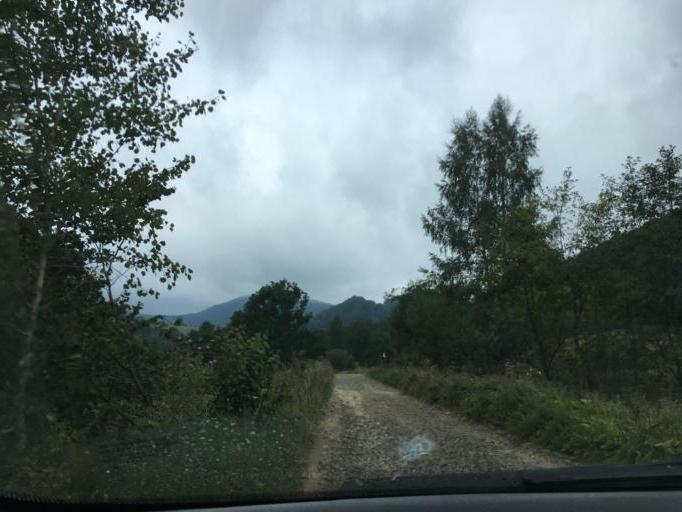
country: PL
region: Subcarpathian Voivodeship
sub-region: Powiat bieszczadzki
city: Lutowiska
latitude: 49.1641
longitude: 22.6228
